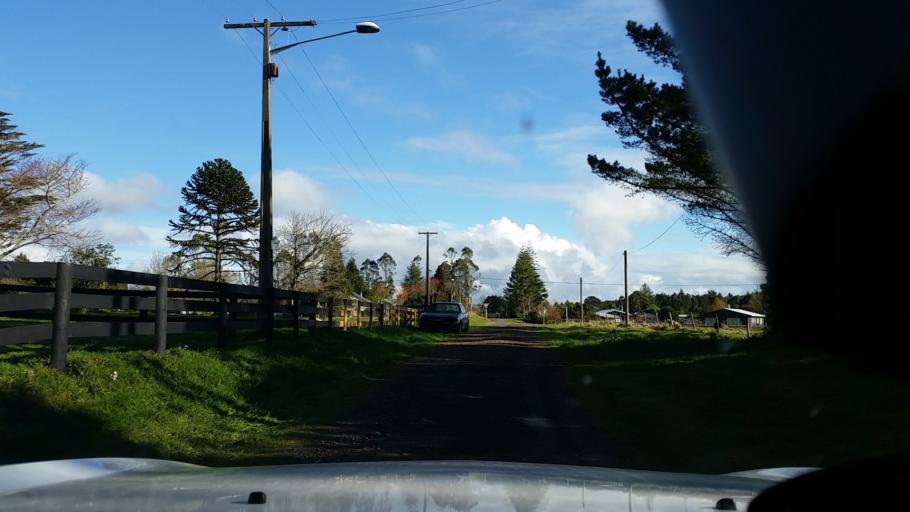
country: NZ
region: Bay of Plenty
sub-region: Rotorua District
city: Rotorua
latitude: -38.0999
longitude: 176.0799
